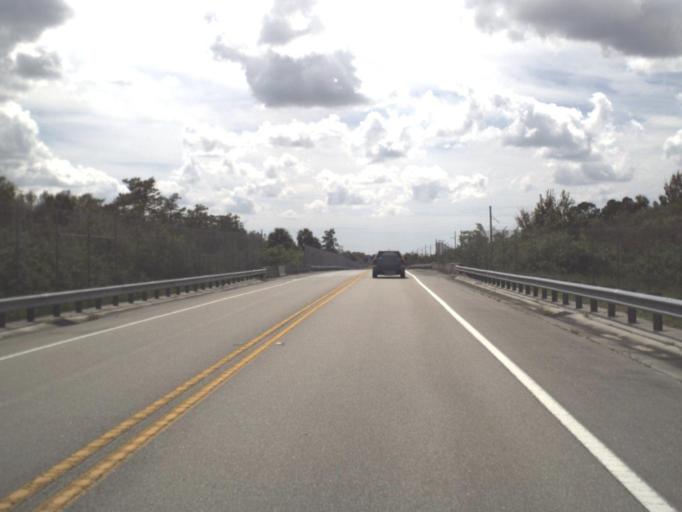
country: US
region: Florida
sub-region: Collier County
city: Lely Resort
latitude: 25.9828
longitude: -81.3488
